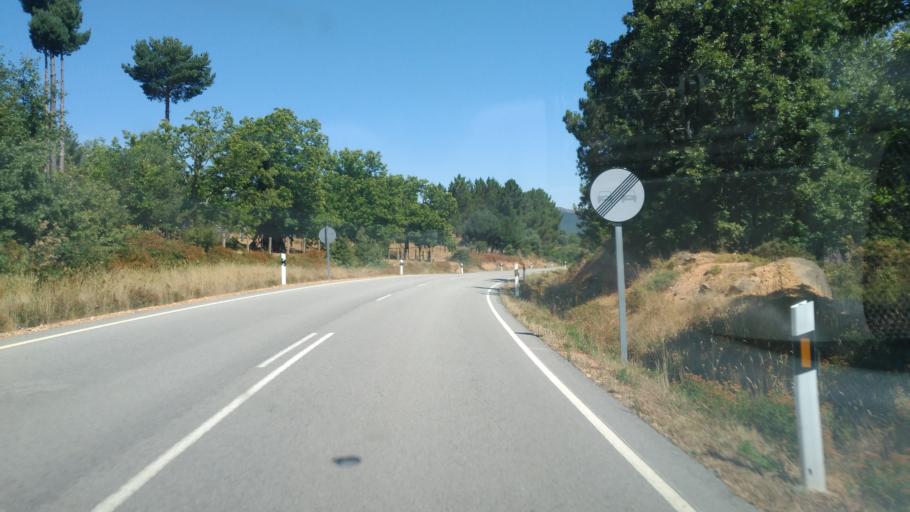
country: ES
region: Castille and Leon
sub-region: Provincia de Salamanca
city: Nava de Francia
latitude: 40.5557
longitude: -6.1337
